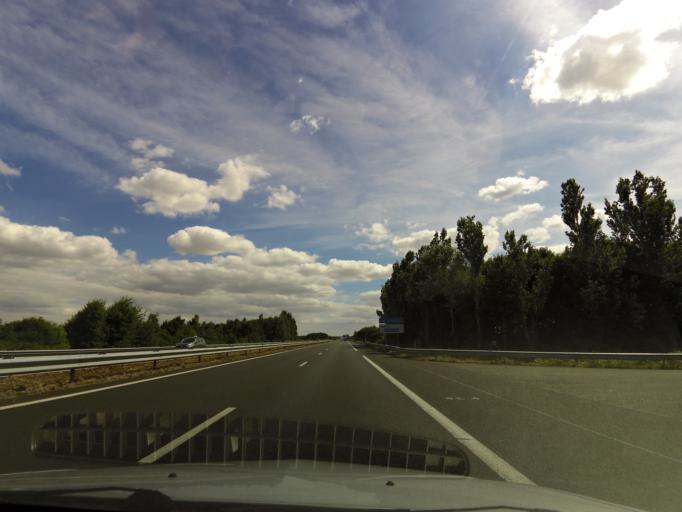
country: FR
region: Pays de la Loire
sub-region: Departement de la Vendee
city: Chauche
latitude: 46.8289
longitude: -1.2248
